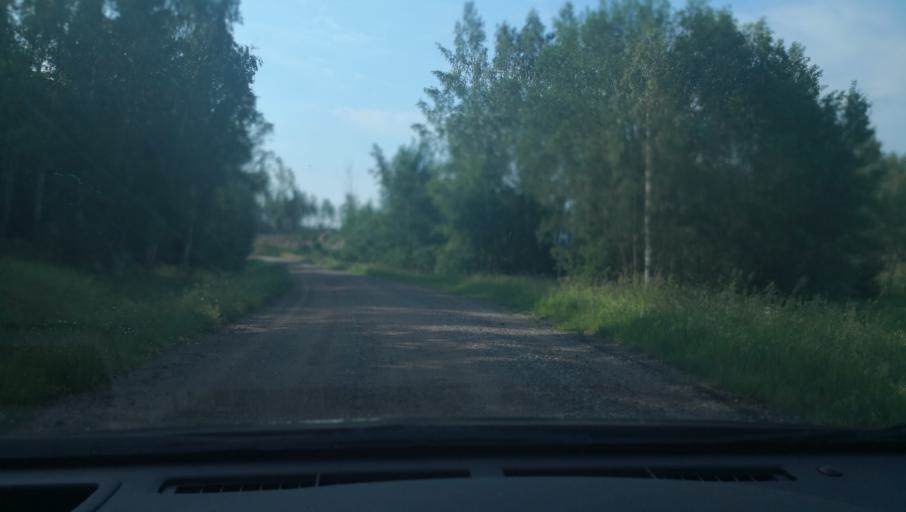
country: SE
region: Vaestmanland
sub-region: Arboga Kommun
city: Tyringe
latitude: 59.3227
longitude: 15.9777
